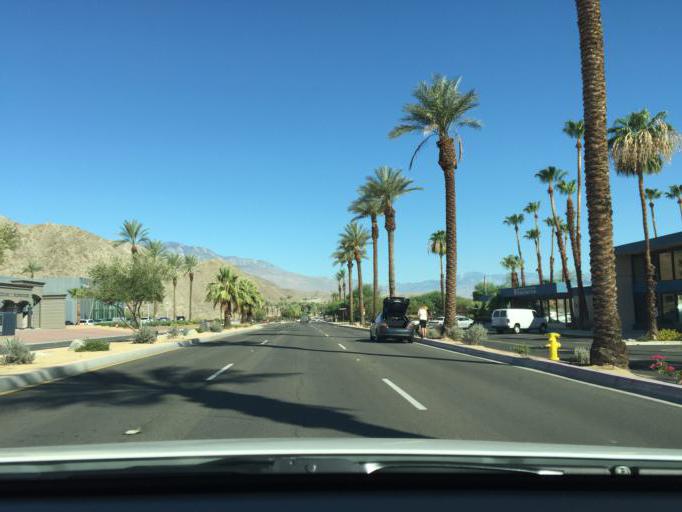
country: US
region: California
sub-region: Riverside County
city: Rancho Mirage
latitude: 33.7466
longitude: -116.4188
